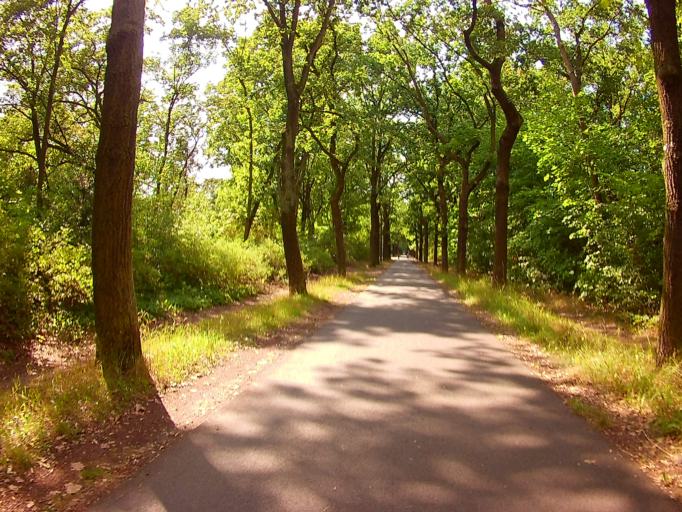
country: DE
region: Berlin
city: Oberschoneweide
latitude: 52.4653
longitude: 13.5313
